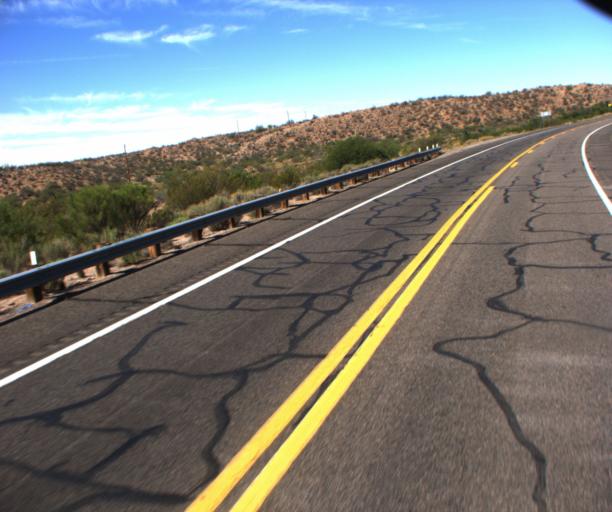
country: US
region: Arizona
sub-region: Yavapai County
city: Congress
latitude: 34.1666
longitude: -112.8370
